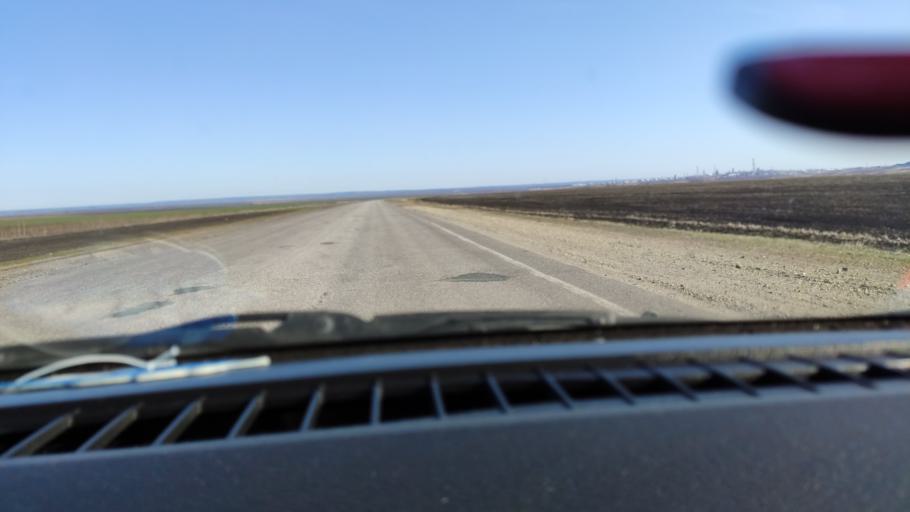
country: RU
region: Samara
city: Varlamovo
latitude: 53.0229
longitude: 48.3335
